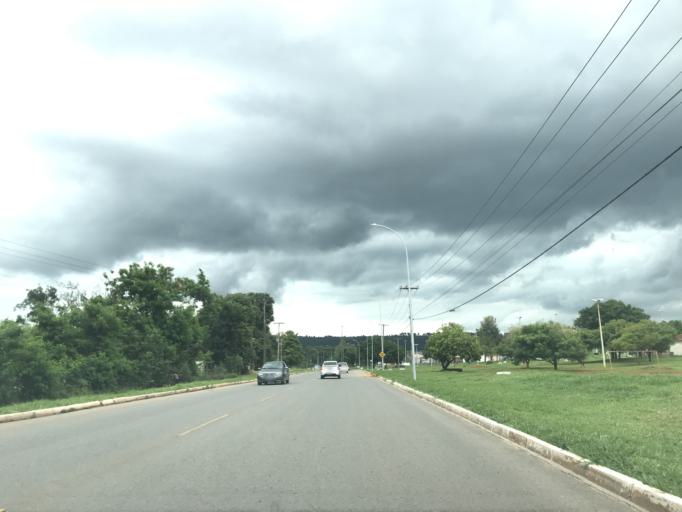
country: BR
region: Federal District
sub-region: Brasilia
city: Brasilia
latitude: -15.6476
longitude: -47.8121
